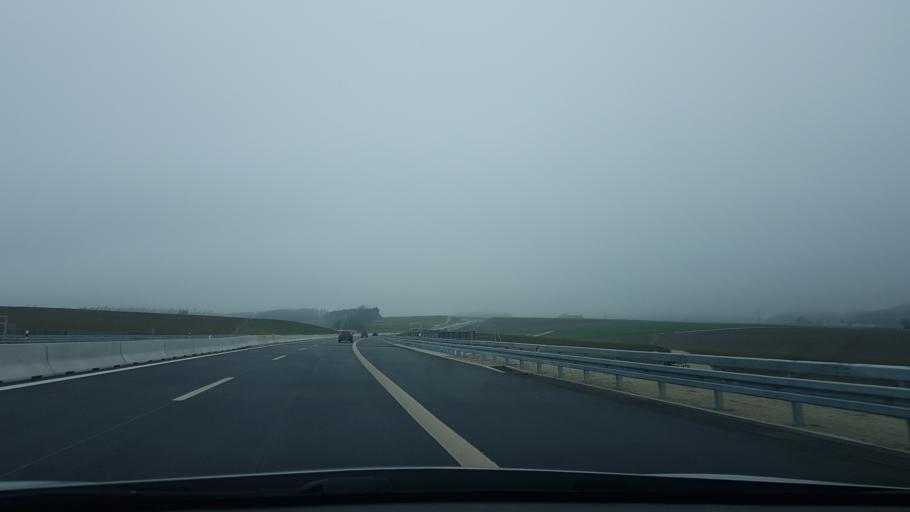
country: DE
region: Bavaria
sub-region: Lower Bavaria
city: Essenbach
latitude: 48.6311
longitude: 12.2075
